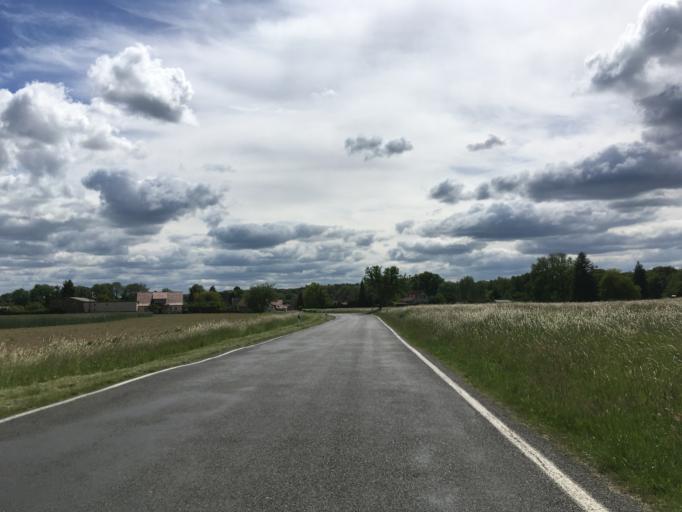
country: DE
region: Brandenburg
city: Protzel
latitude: 52.6909
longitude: 14.0111
